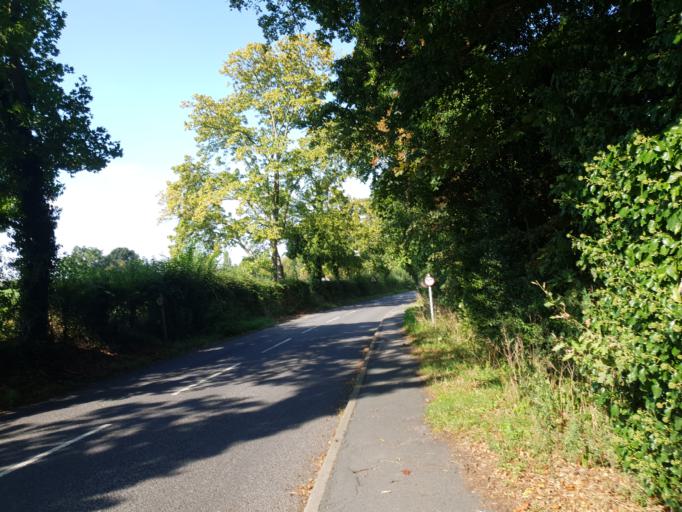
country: GB
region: England
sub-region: Suffolk
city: East Bergholt
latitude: 51.9489
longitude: 0.9955
